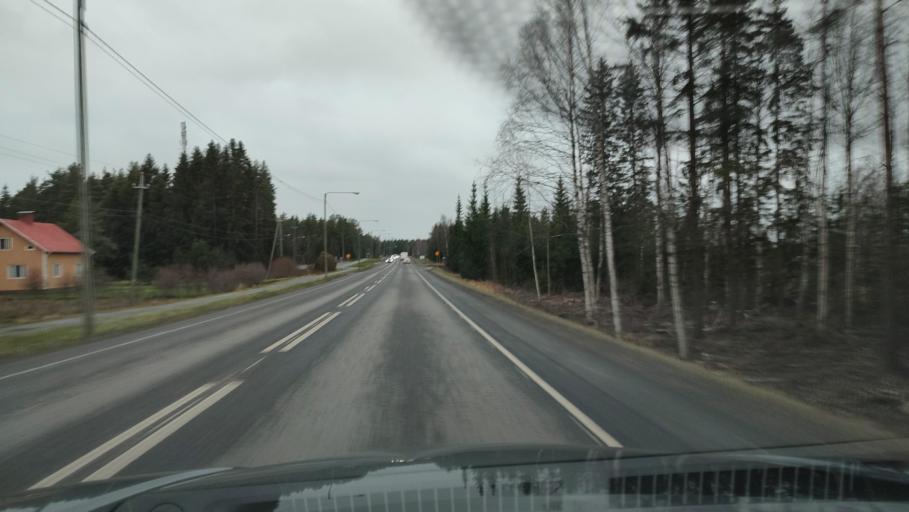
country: FI
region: Southern Ostrobothnia
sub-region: Seinaejoki
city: Seinaejoki
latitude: 62.7794
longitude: 22.6987
